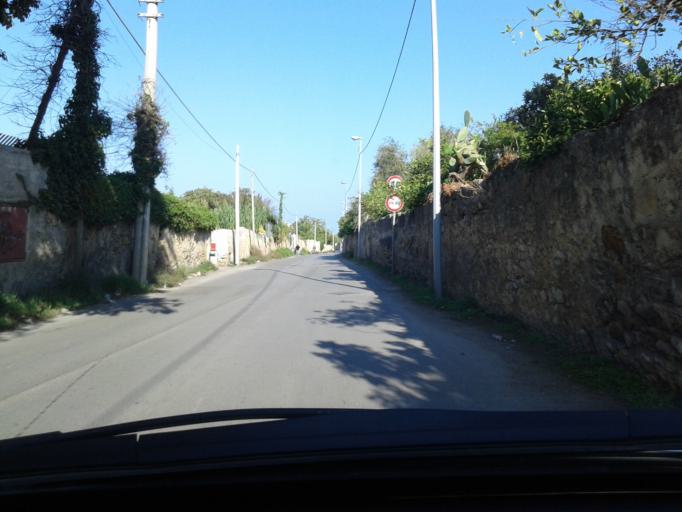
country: IT
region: Sicily
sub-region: Palermo
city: Palermo
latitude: 38.1039
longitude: 13.3214
